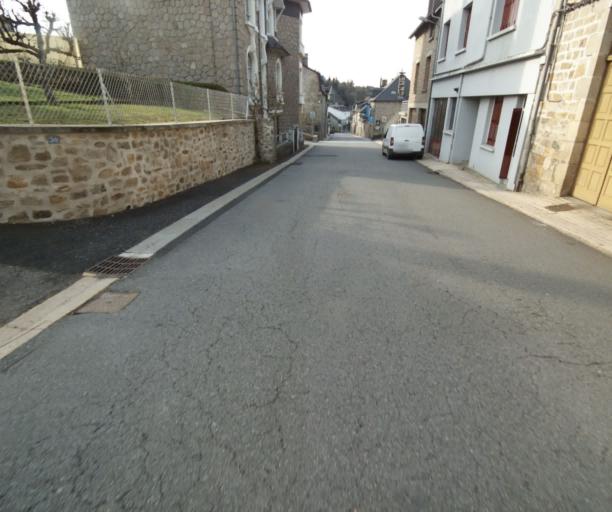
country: FR
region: Limousin
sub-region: Departement de la Correze
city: Correze
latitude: 45.3738
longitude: 1.8741
